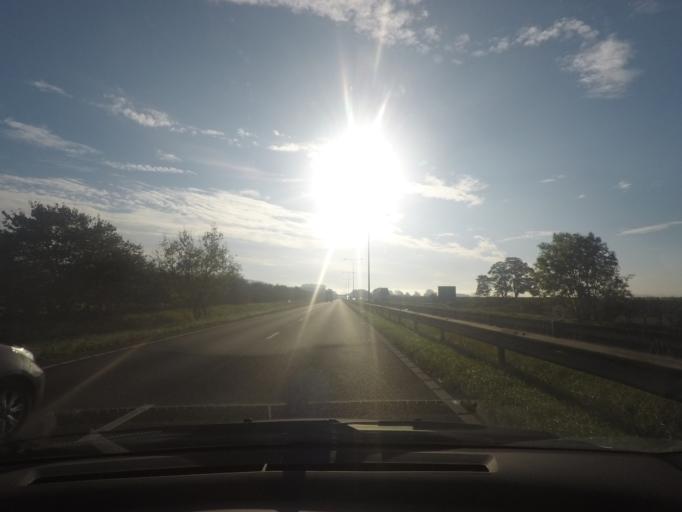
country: GB
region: England
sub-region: East Riding of Yorkshire
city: Brantingham
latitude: 53.7546
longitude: -0.5834
